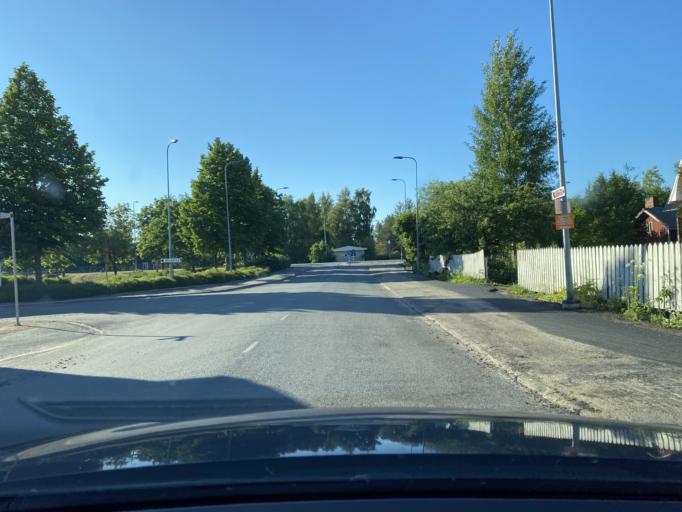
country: FI
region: Satakunta
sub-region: Pori
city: Huittinen
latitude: 61.1738
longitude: 22.6946
